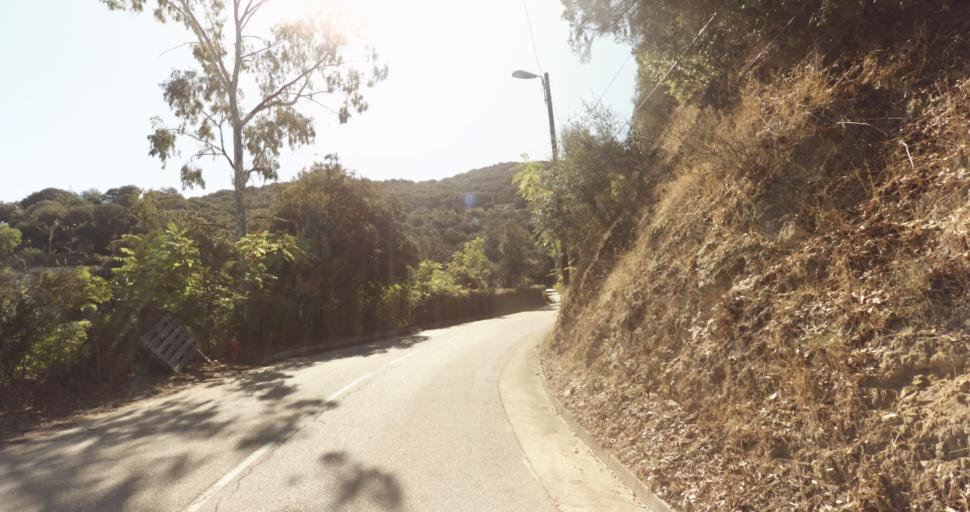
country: FR
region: Corsica
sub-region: Departement de la Corse-du-Sud
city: Ajaccio
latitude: 41.9259
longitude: 8.7084
